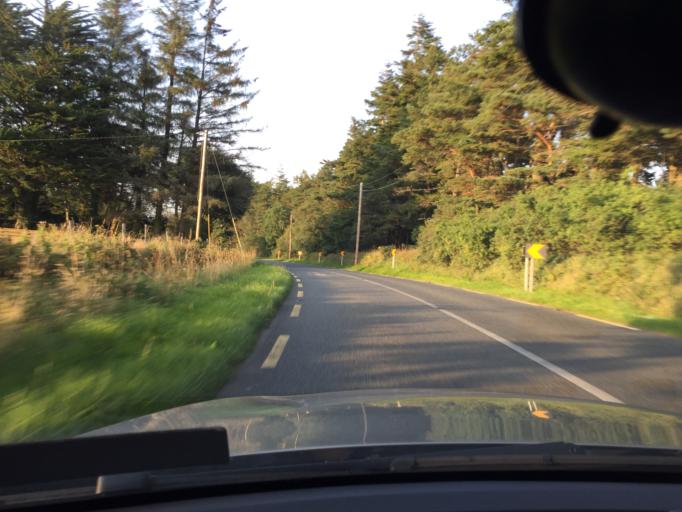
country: IE
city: Newtownmountkennedy
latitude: 53.0776
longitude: -6.2134
